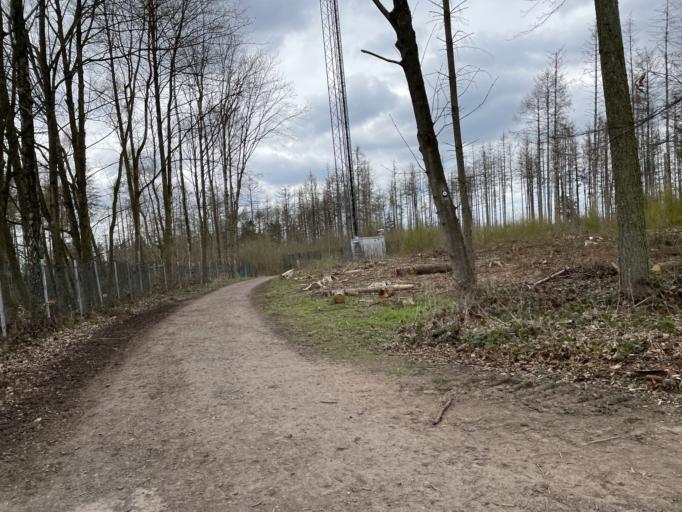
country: DE
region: North Rhine-Westphalia
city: Porta Westfalica
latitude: 52.2276
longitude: 8.9330
